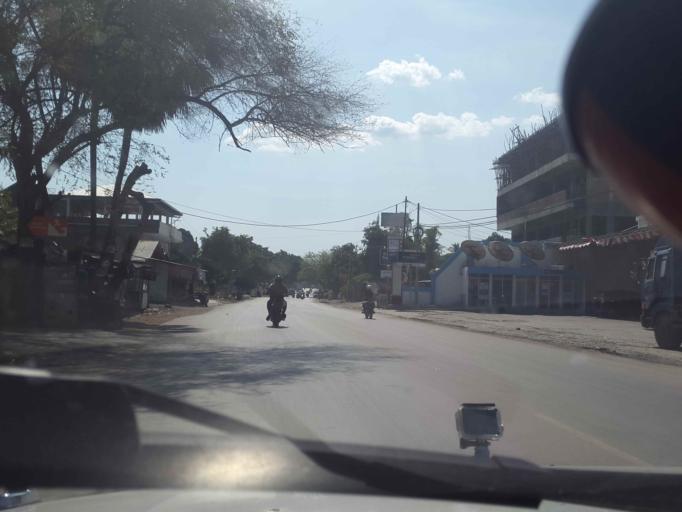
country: ID
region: East Nusa Tenggara
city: Oesapa
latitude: -10.1489
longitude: 123.6478
